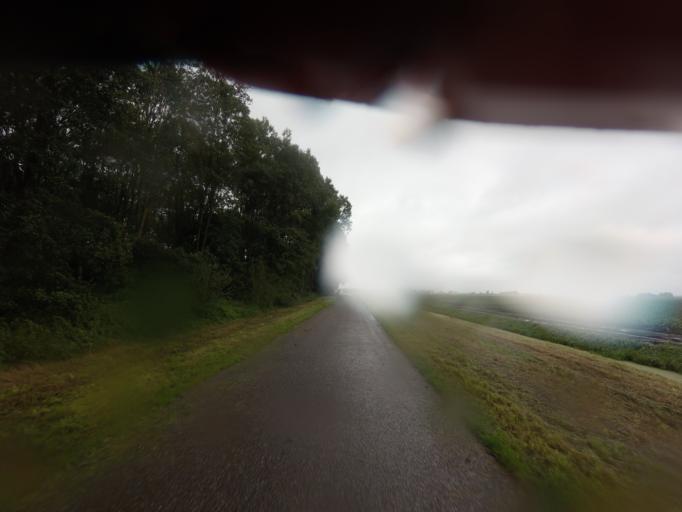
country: NL
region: North Holland
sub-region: Gemeente Medemblik
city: Opperdoes
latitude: 52.7156
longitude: 5.0980
